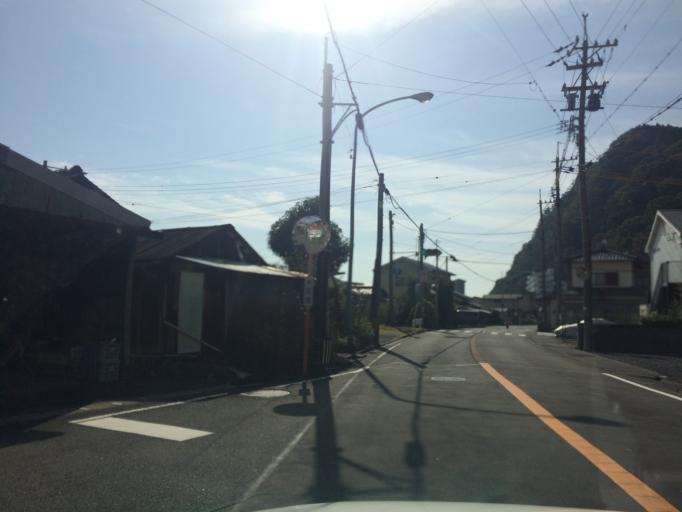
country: JP
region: Shizuoka
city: Yaizu
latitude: 34.9152
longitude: 138.3555
